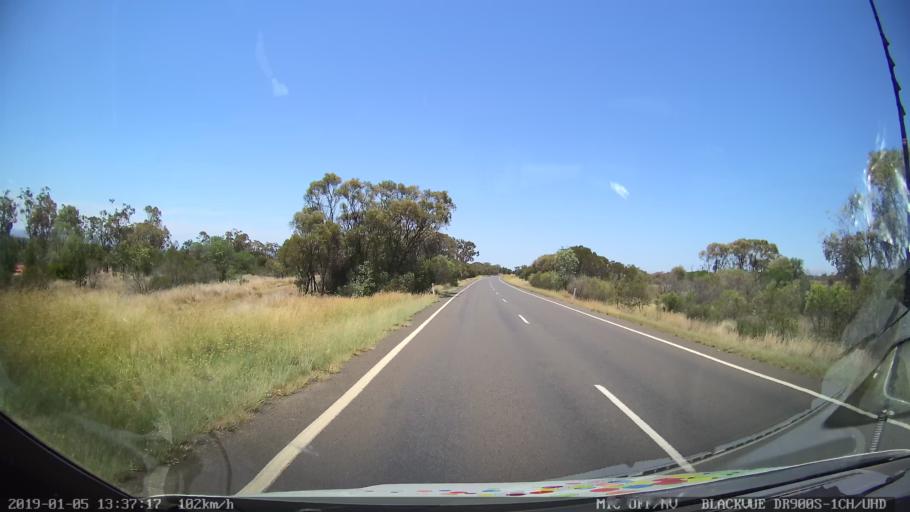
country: AU
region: New South Wales
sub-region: Gunnedah
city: Gunnedah
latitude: -30.9819
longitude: 150.1789
